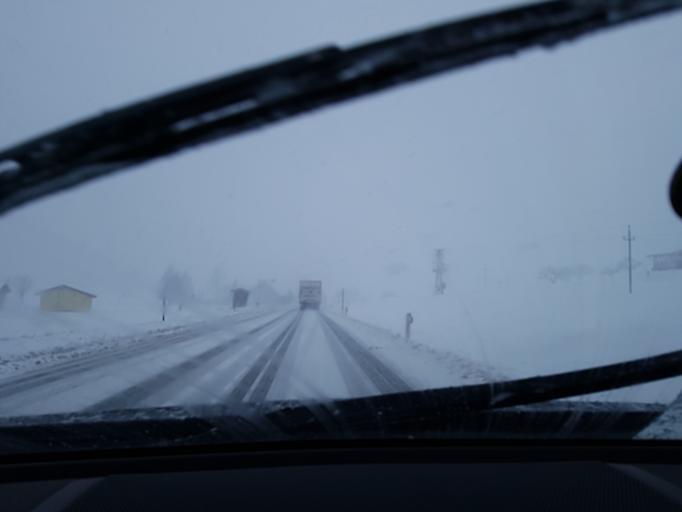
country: AT
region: Salzburg
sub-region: Politischer Bezirk Hallein
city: Abtenau
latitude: 47.5741
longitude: 13.3298
